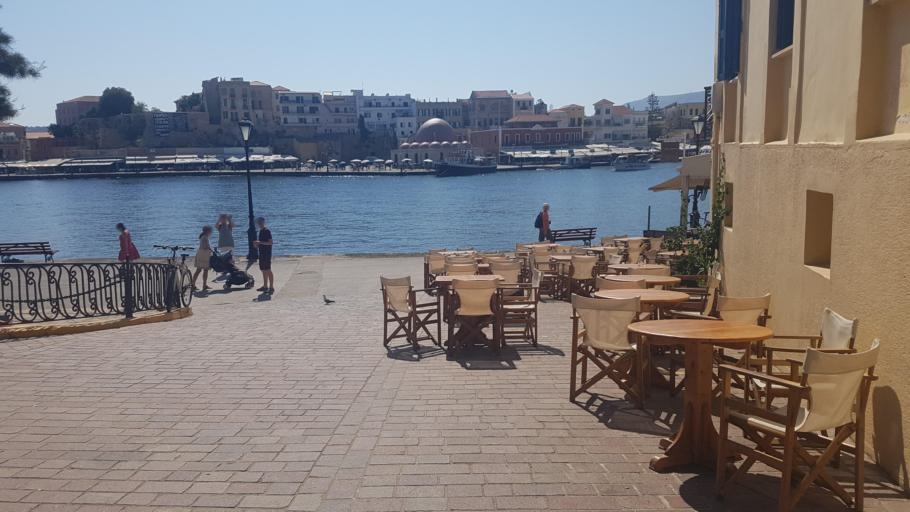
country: GR
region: Crete
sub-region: Nomos Chanias
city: Chania
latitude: 35.5178
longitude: 24.0157
